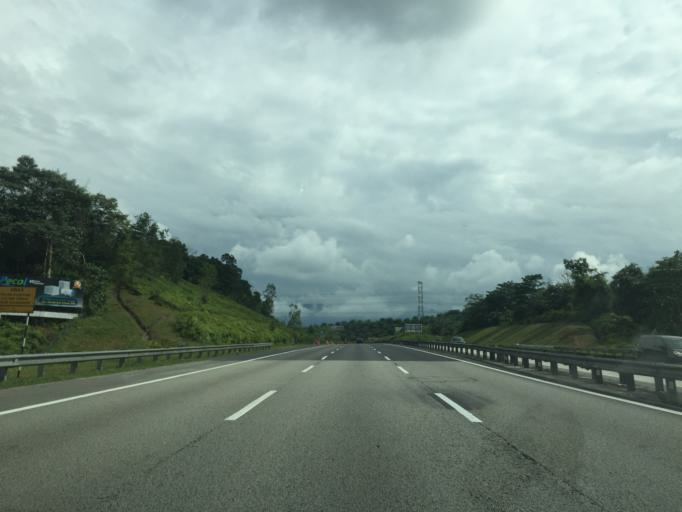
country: MY
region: Selangor
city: Batang Berjuntai
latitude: 3.5977
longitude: 101.5194
